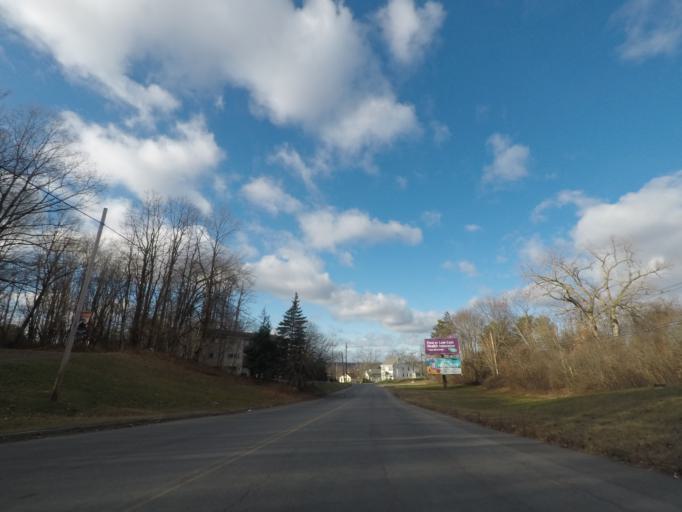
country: US
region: New York
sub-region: Saratoga County
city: Waterford
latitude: 42.7871
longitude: -73.6599
